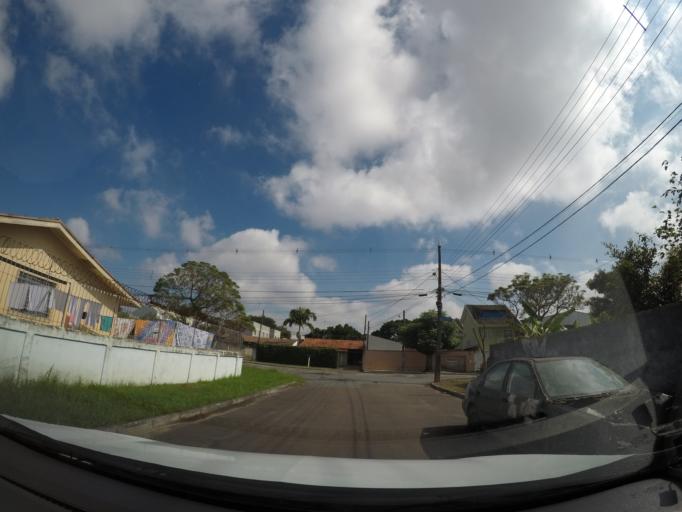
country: BR
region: Parana
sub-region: Sao Jose Dos Pinhais
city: Sao Jose dos Pinhais
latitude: -25.4951
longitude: -49.2239
